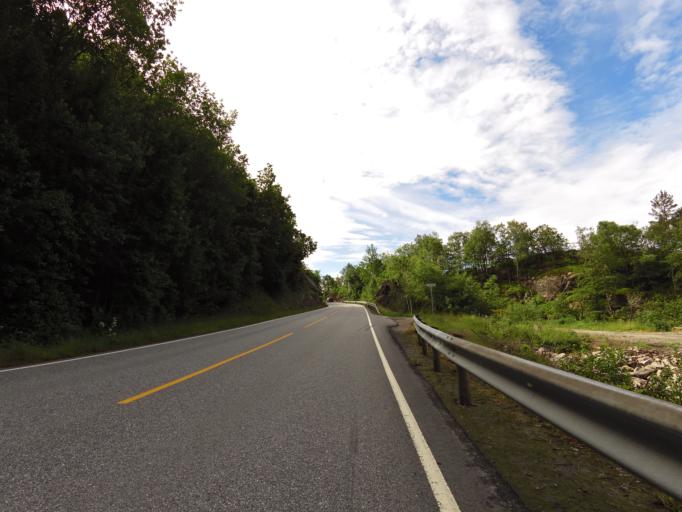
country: NO
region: Vest-Agder
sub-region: Lindesnes
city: Vigeland
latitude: 58.0553
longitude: 7.1818
